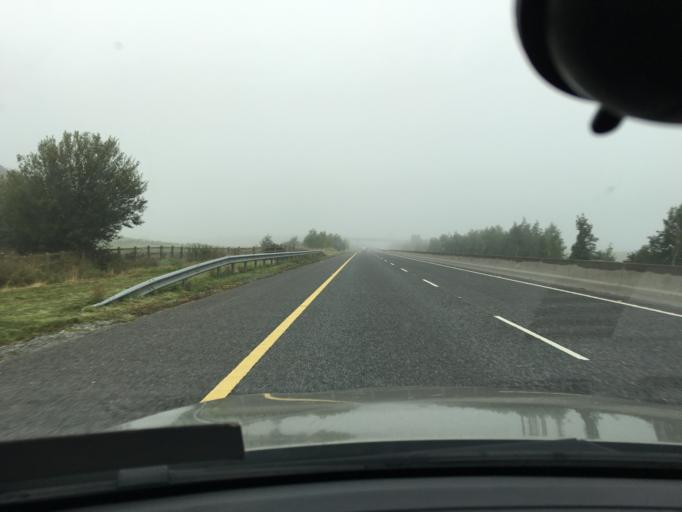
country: IE
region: Leinster
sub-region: An Iarmhi
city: Moate
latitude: 53.3856
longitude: -7.7039
